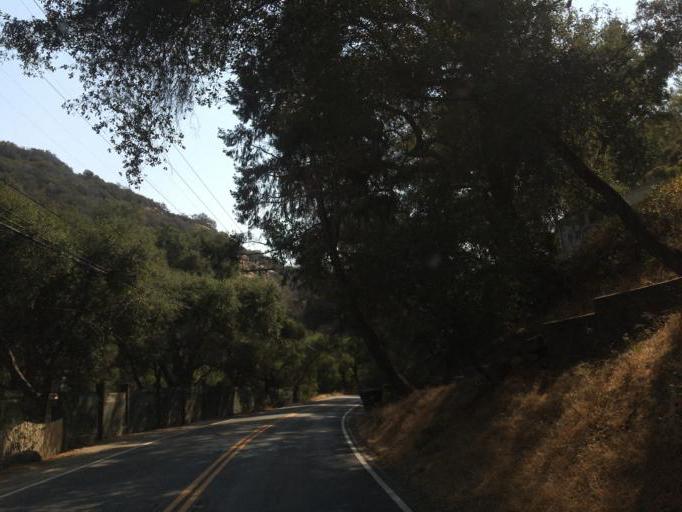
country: US
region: California
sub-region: Los Angeles County
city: Topanga
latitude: 34.1043
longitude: -118.6252
